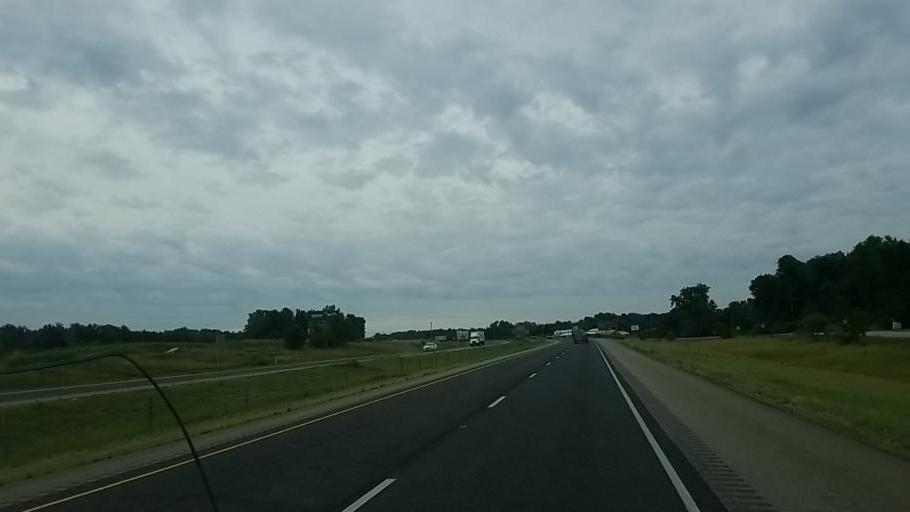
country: US
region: Indiana
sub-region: Steuben County
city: Fremont
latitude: 41.7183
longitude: -85.0023
